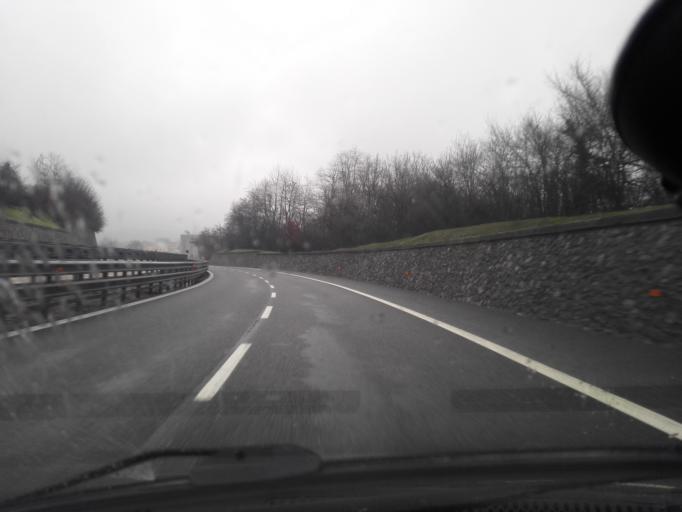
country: IT
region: Piedmont
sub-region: Provincia di Alessandria
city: Stazzano
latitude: 44.7109
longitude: 8.8705
